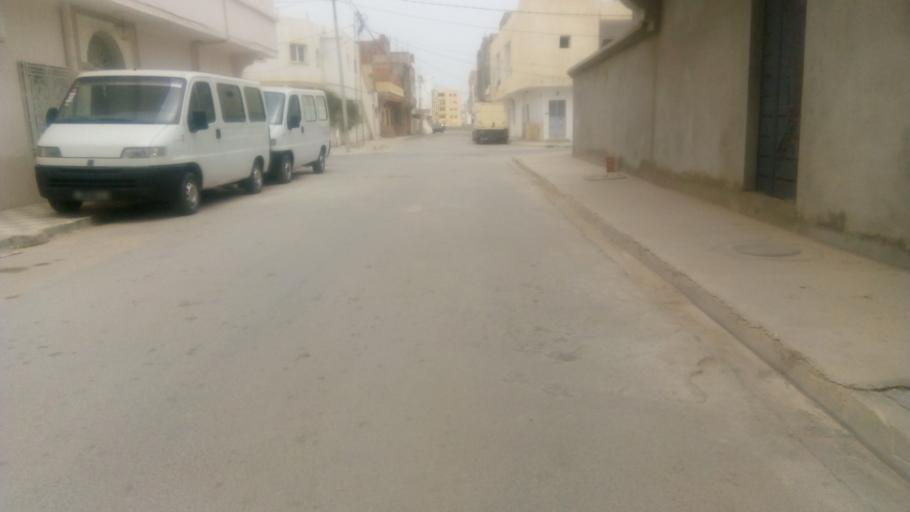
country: TN
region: Al Qayrawan
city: Kairouan
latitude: 35.6686
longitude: 10.0883
